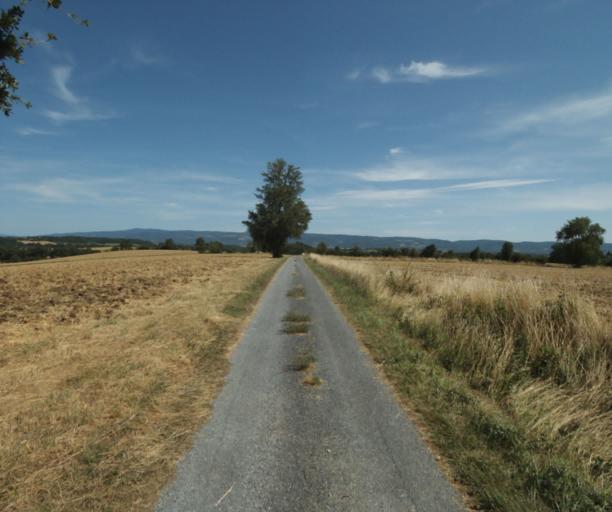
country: FR
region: Midi-Pyrenees
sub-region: Departement du Tarn
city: Puylaurens
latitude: 43.5389
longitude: 2.0167
